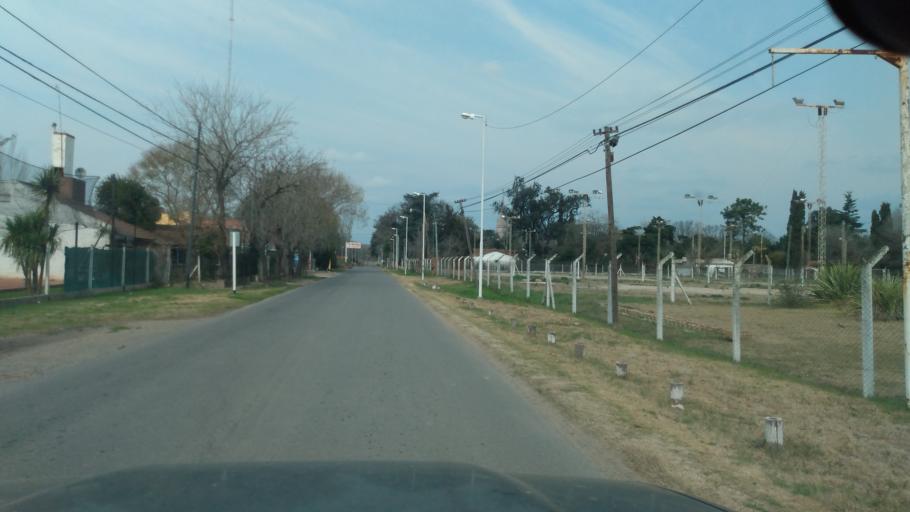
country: AR
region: Buenos Aires
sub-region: Partido de Lujan
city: Lujan
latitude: -34.5559
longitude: -59.1253
